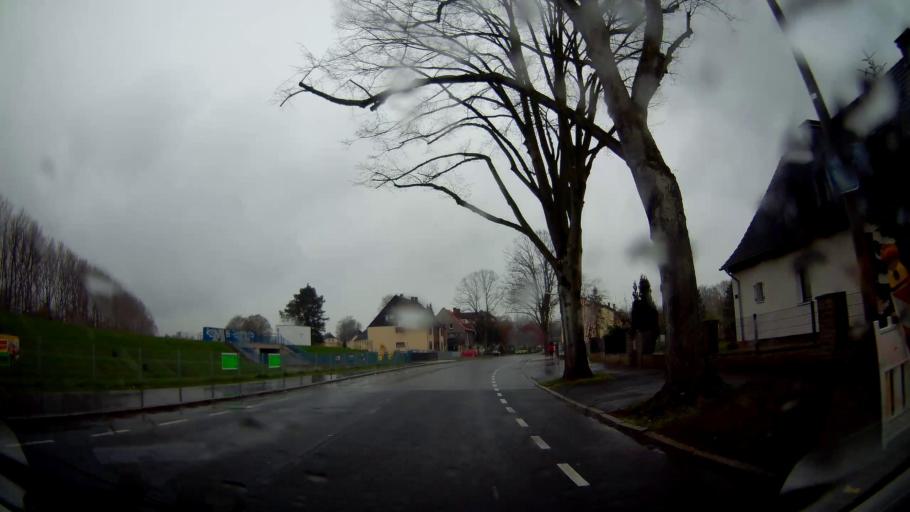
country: DE
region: North Rhine-Westphalia
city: Witten
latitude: 51.5088
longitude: 7.3756
